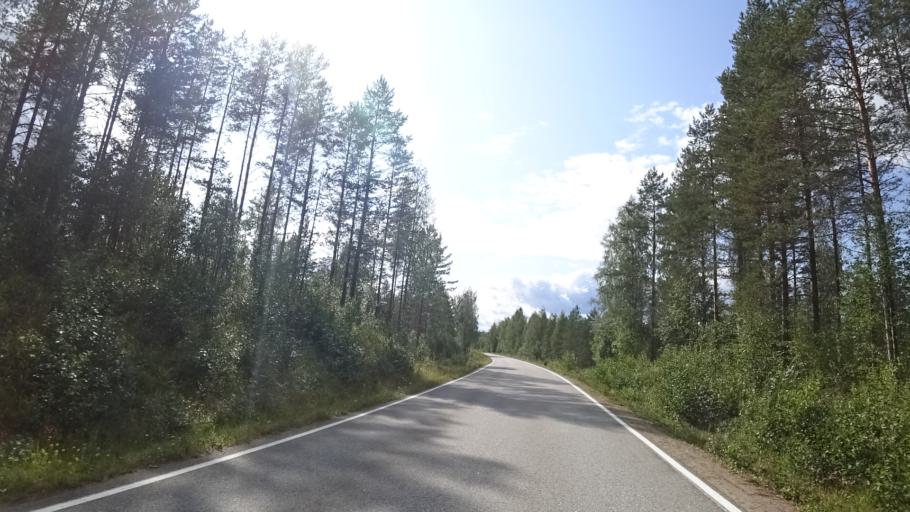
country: FI
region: North Karelia
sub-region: Joensuu
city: Ilomantsi
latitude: 62.4124
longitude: 30.9798
